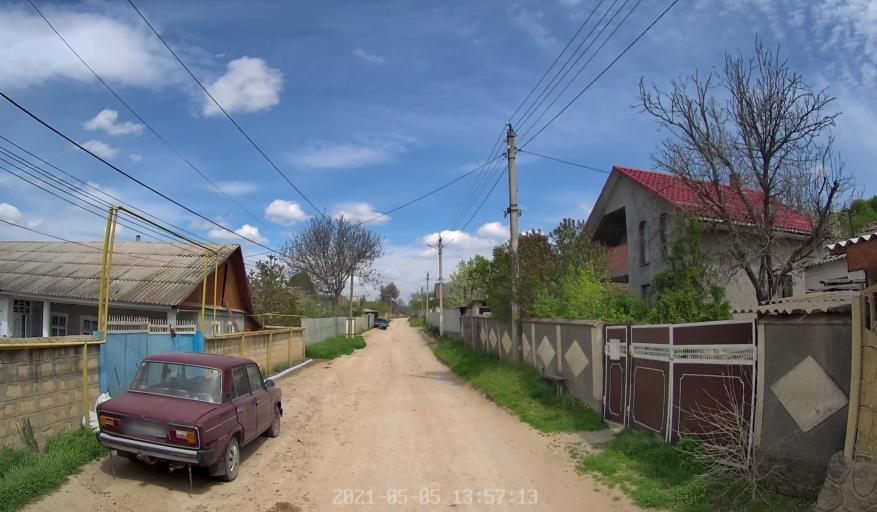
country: MD
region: Chisinau
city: Vadul lui Voda
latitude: 47.0632
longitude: 29.1348
